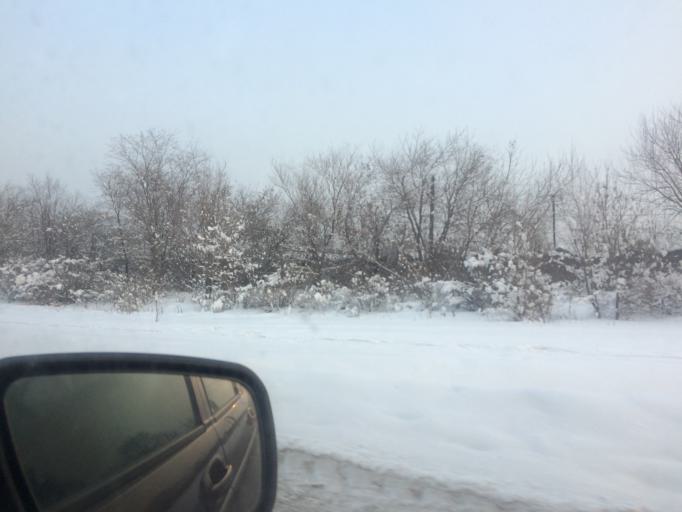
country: RU
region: Chelyabinsk
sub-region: Gorod Magnitogorsk
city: Magnitogorsk
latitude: 53.4627
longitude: 59.0672
